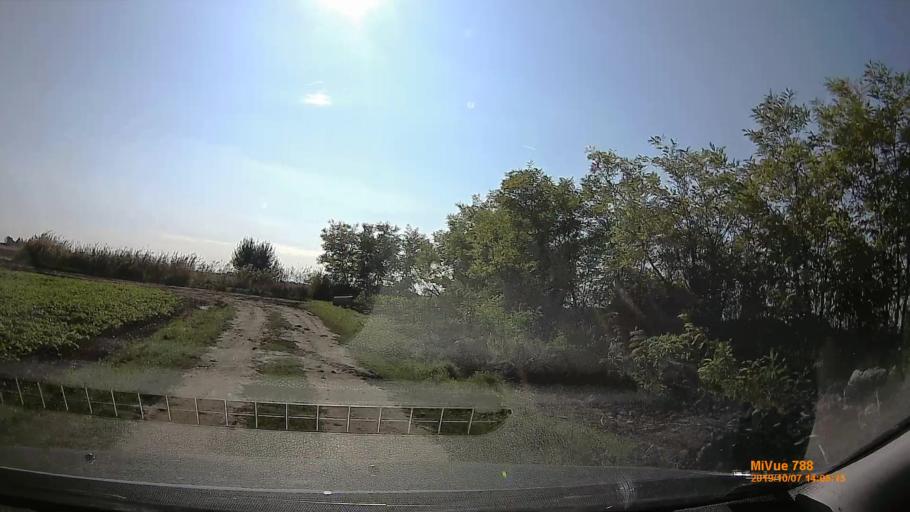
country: HU
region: Jasz-Nagykun-Szolnok
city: Cserkeszolo
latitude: 46.8700
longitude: 20.2241
